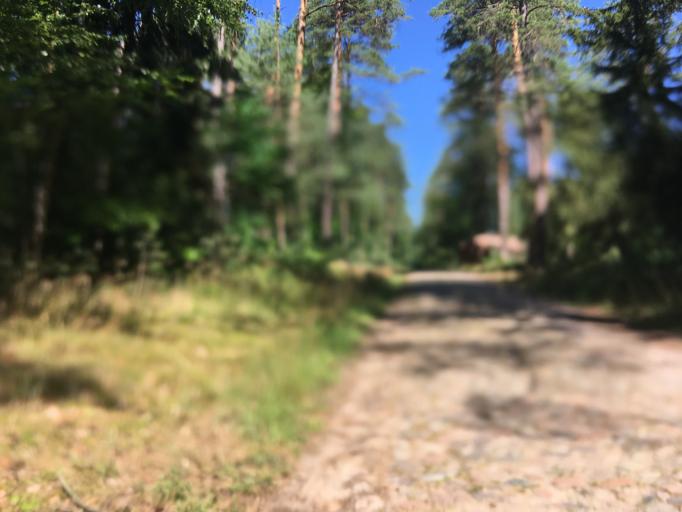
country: DE
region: Brandenburg
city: Rheinsberg
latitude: 53.1100
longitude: 12.9568
